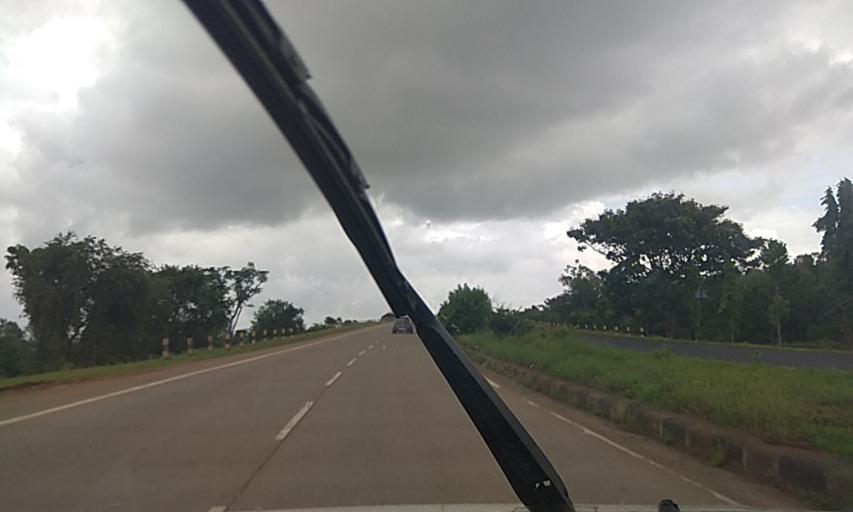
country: IN
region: Karnataka
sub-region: Belgaum
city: Sankeshwar
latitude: 16.2776
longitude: 74.4503
